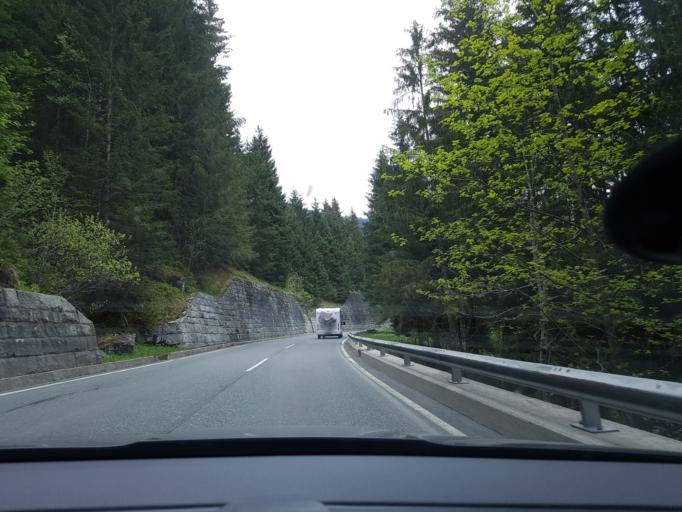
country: AT
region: Salzburg
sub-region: Politischer Bezirk Zell am See
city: Krimml
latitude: 47.2164
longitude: 12.1629
